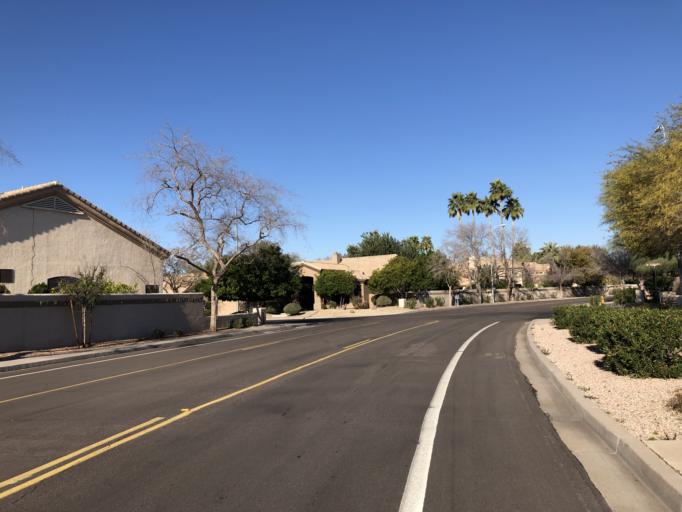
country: US
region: Arizona
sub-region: Maricopa County
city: San Carlos
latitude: 33.3158
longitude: -111.9128
